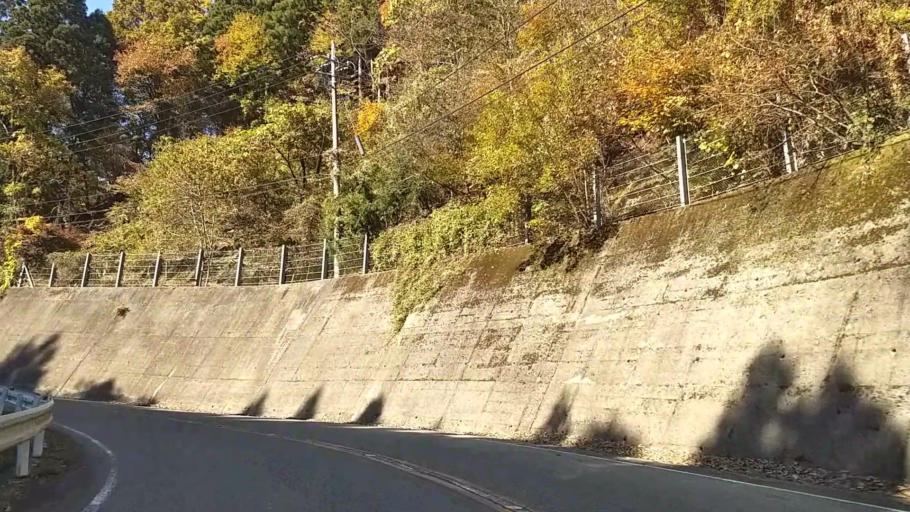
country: JP
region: Yamanashi
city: Otsuki
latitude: 35.7294
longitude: 138.9820
